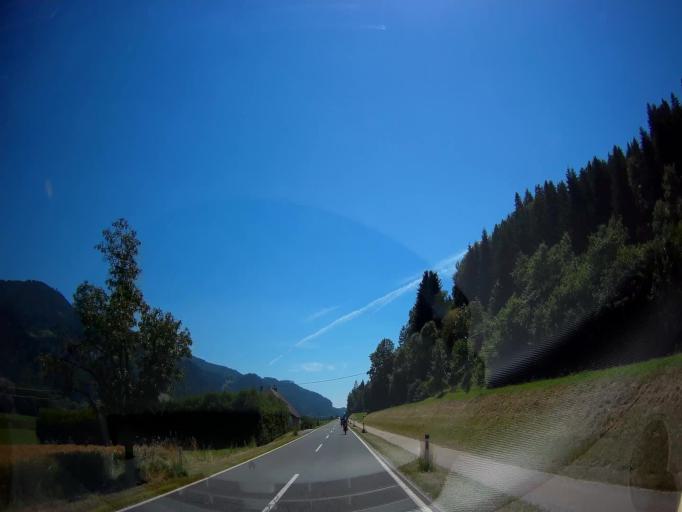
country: AT
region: Carinthia
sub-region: Politischer Bezirk Sankt Veit an der Glan
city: Micheldorf
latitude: 46.9356
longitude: 14.4240
